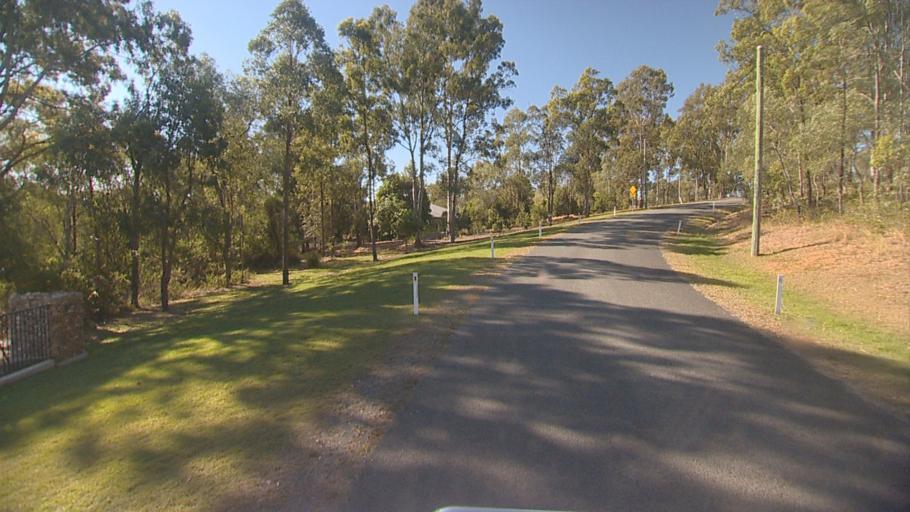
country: AU
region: Queensland
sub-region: Logan
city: Windaroo
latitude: -27.7620
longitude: 153.1451
